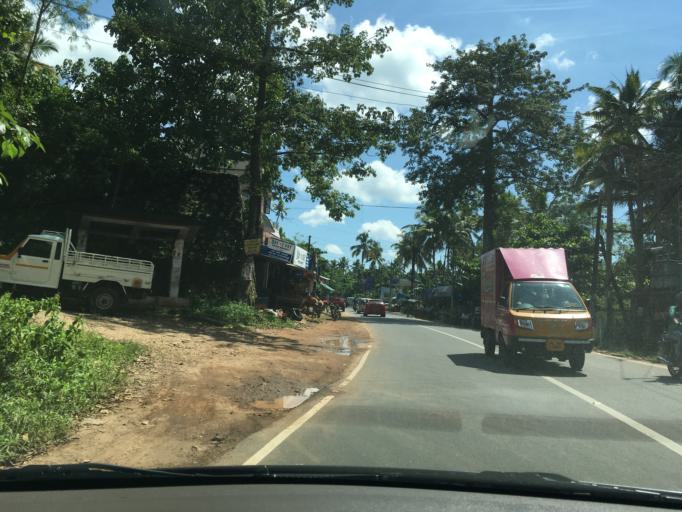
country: IN
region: Kerala
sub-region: Thiruvananthapuram
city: Nedumangad
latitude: 8.5935
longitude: 76.9952
